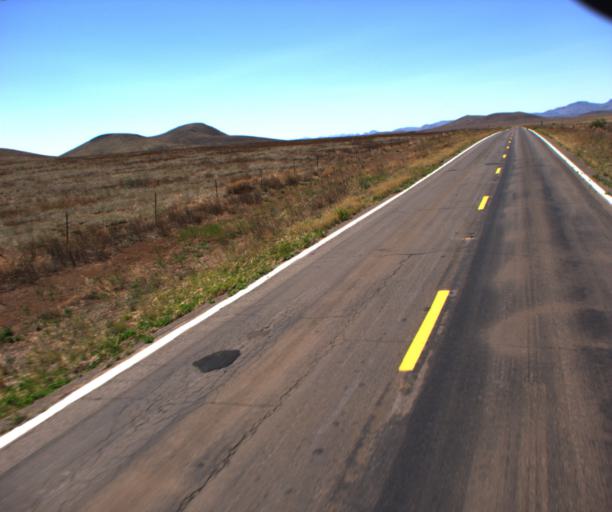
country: US
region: Arizona
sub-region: Cochise County
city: Douglas
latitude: 31.5910
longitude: -109.2426
